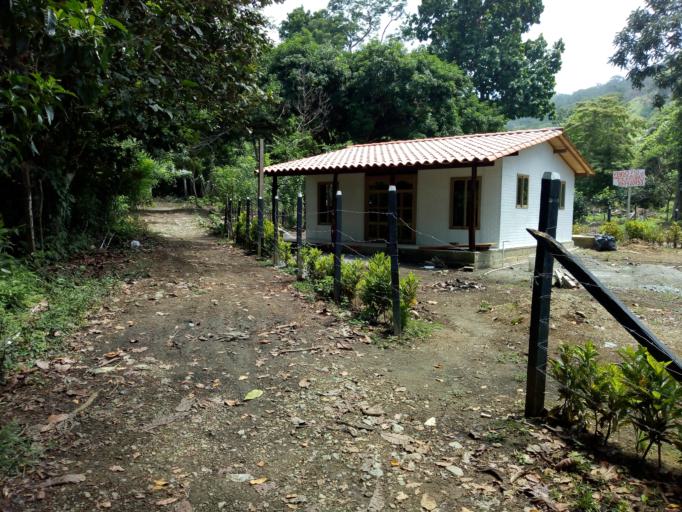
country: PA
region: Guna Yala
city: Puerto Obaldia
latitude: 8.6269
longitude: -77.3580
